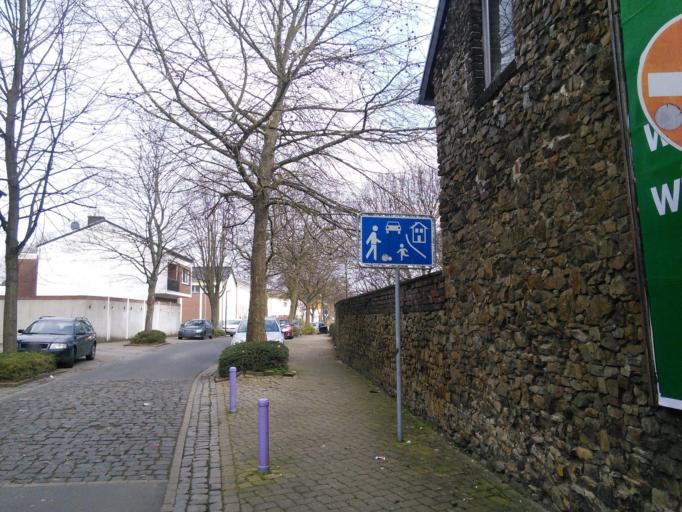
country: DE
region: North Rhine-Westphalia
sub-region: Regierungsbezirk Koln
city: Langerwehe
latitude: 50.8168
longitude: 6.3636
